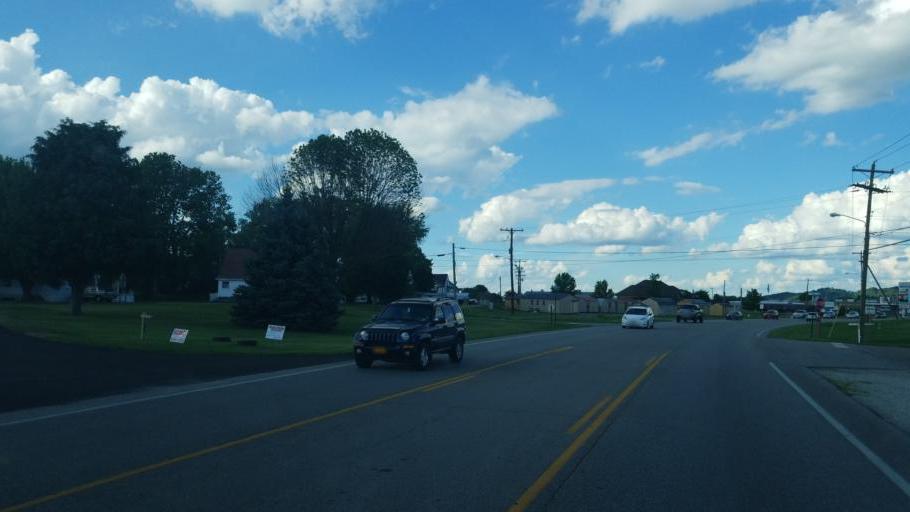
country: US
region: West Virginia
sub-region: Mason County
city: Point Pleasant
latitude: 38.8276
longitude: -82.1664
